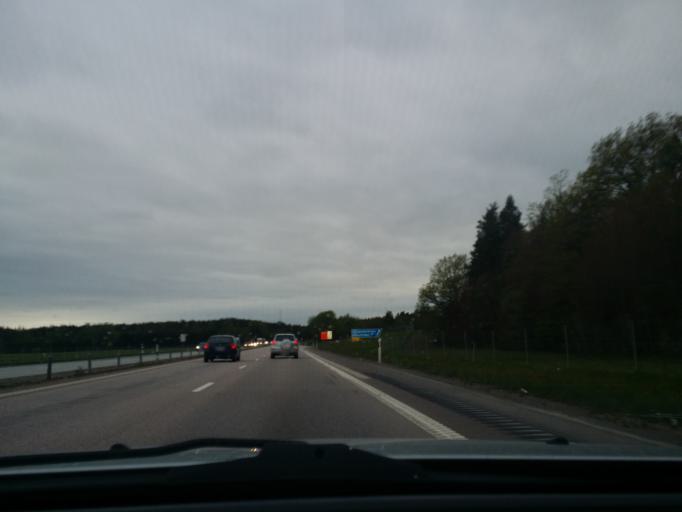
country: SE
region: Vaestmanland
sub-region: Hallstahammars Kommun
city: Kolback
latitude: 59.5836
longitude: 16.3680
